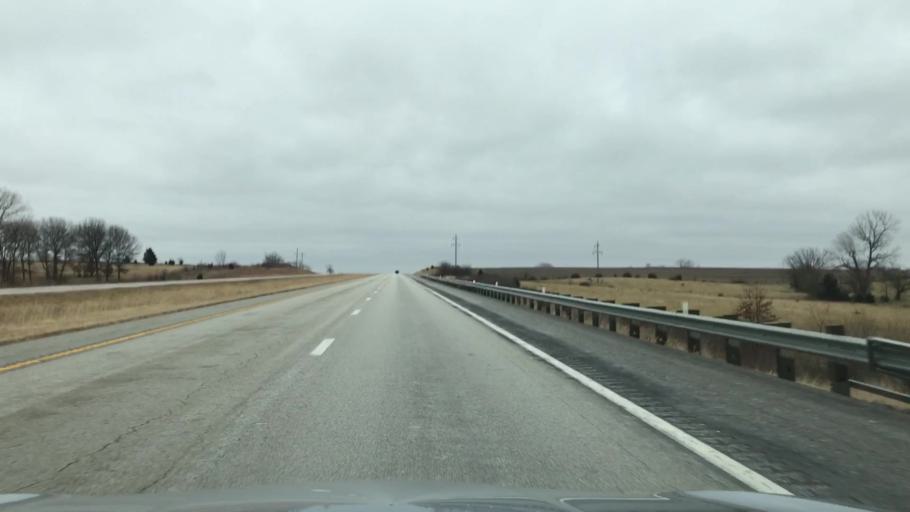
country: US
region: Missouri
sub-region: Caldwell County
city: Hamilton
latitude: 39.7497
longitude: -94.0901
